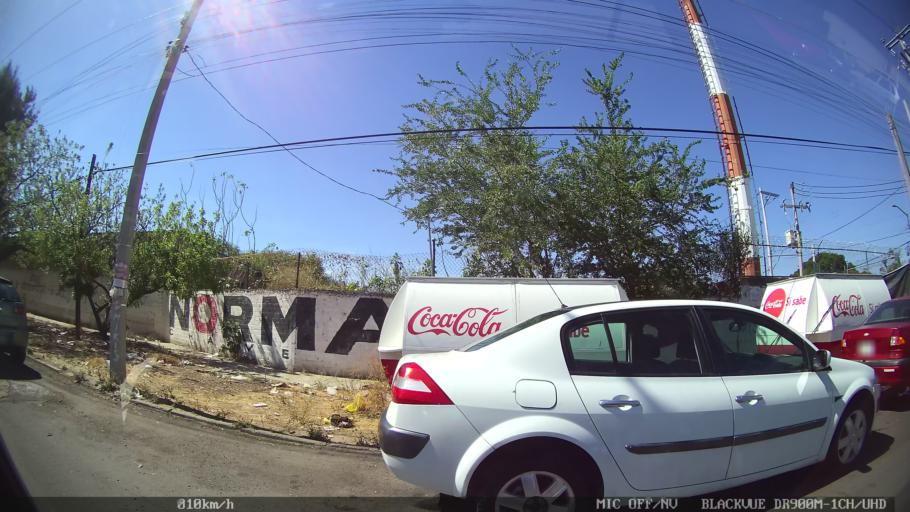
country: MX
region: Jalisco
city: Tlaquepaque
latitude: 20.6517
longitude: -103.2912
